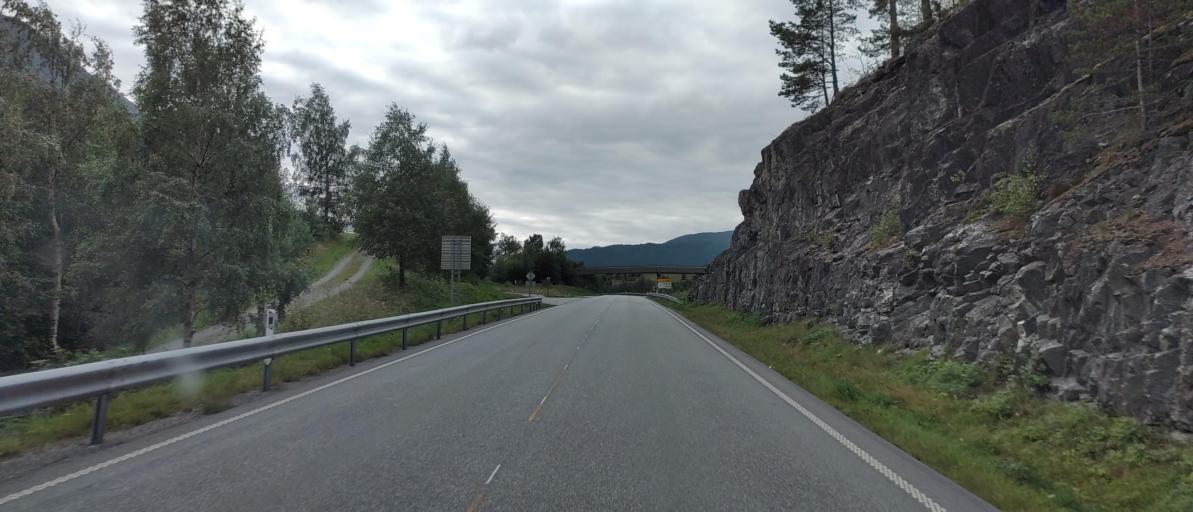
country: NO
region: More og Romsdal
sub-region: Rauma
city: Andalsnes
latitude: 62.5388
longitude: 7.7267
